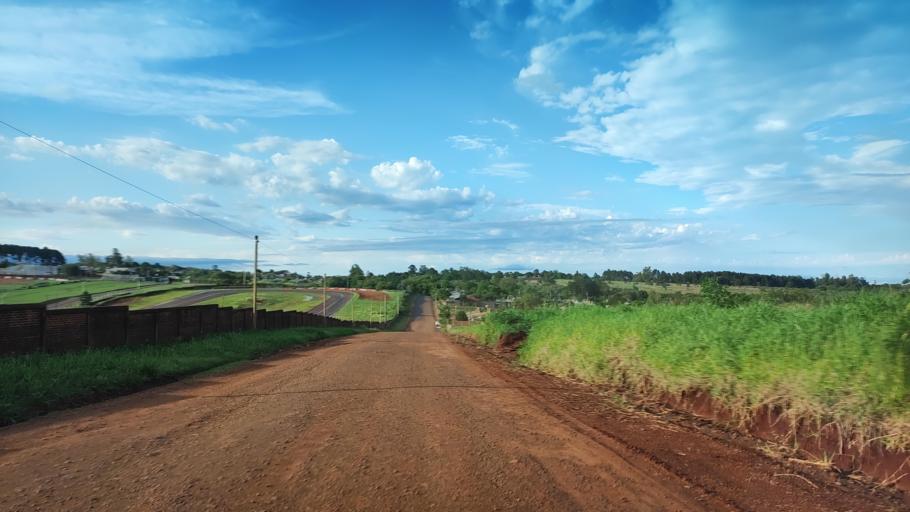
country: AR
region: Misiones
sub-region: Departamento de Capital
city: Posadas
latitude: -27.4392
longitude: -55.9242
